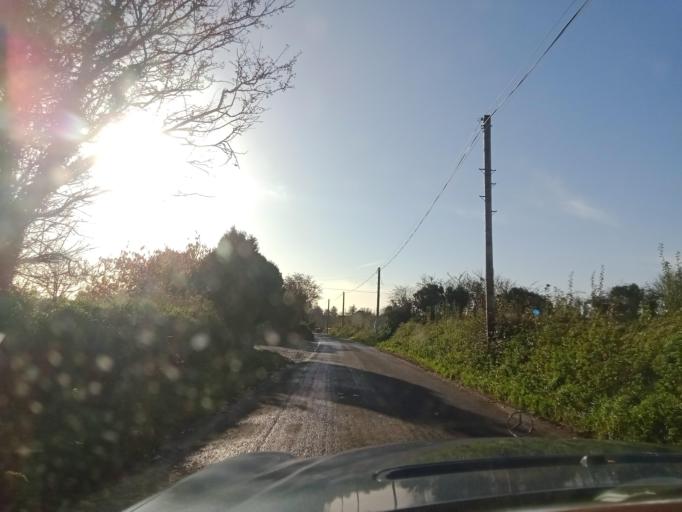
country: IE
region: Leinster
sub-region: Kilkenny
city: Mooncoin
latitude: 52.2809
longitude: -7.2384
